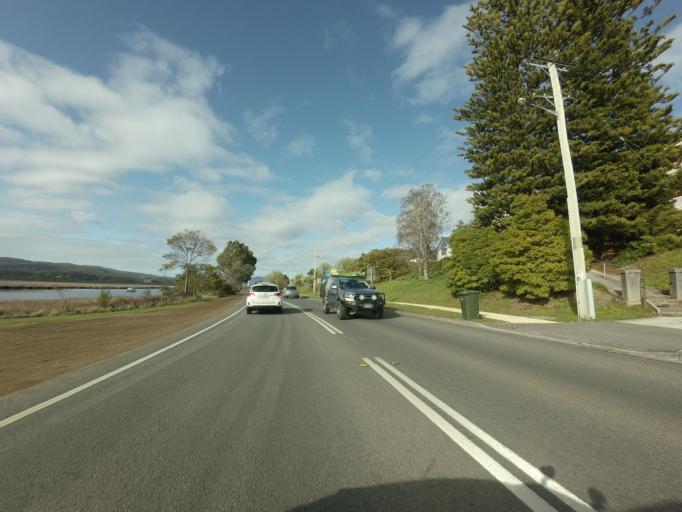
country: AU
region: Tasmania
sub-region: Huon Valley
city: Franklin
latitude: -43.0945
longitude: 147.0075
